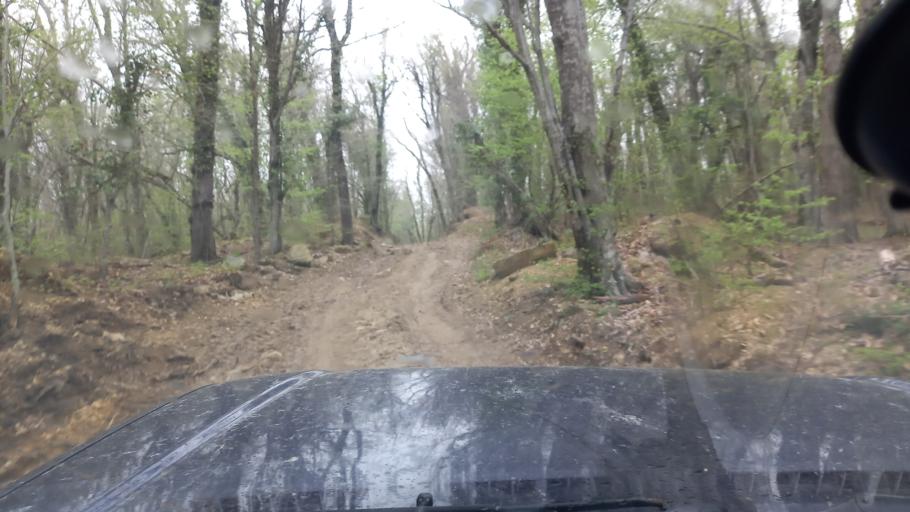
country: RU
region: Krasnodarskiy
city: Dzhubga
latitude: 44.3125
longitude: 38.6798
